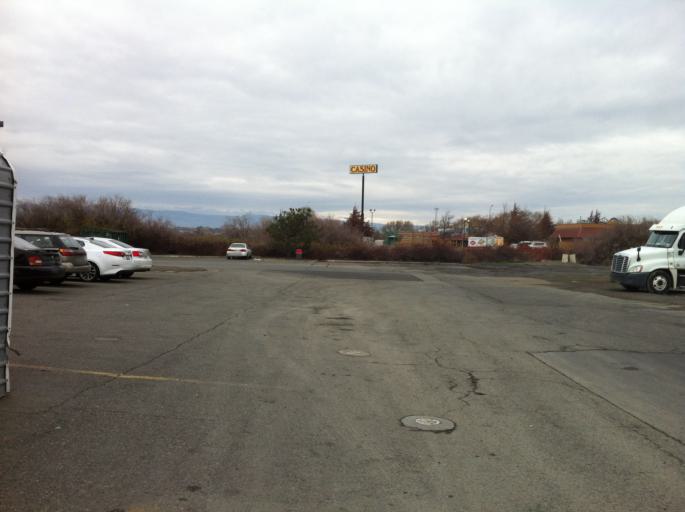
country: US
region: Washington
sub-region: Kittitas County
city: Ellensburg
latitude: 47.0076
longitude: -120.5856
